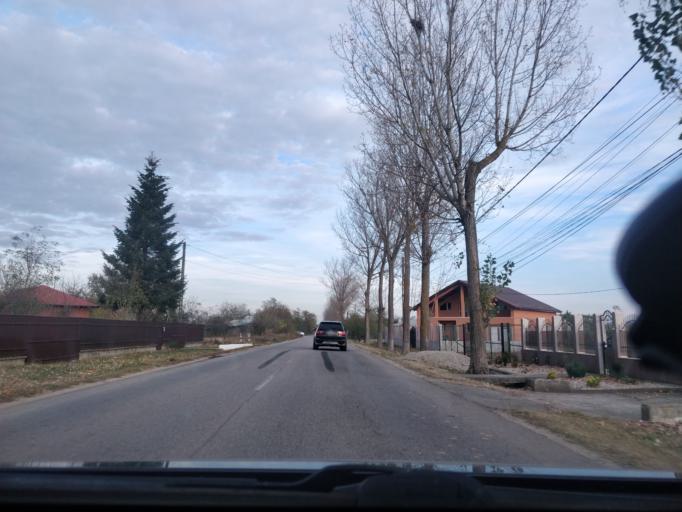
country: RO
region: Giurgiu
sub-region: Comuna Crevedia Mare
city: Crevedia Mare
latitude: 44.4311
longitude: 25.6431
